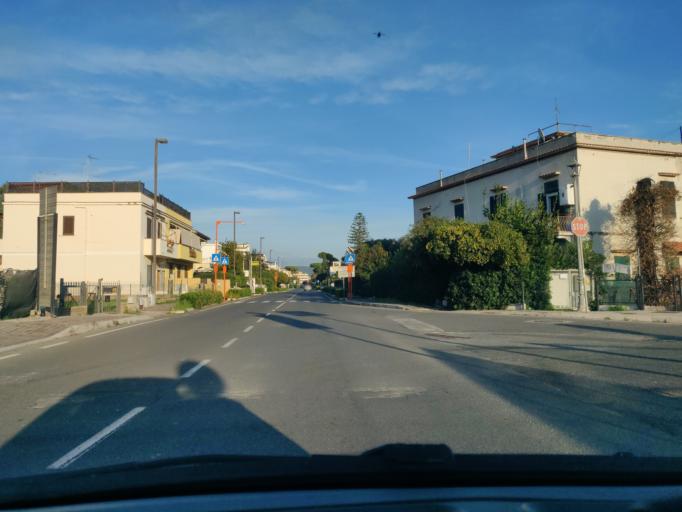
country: IT
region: Latium
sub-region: Citta metropolitana di Roma Capitale
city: Santa Marinella
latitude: 42.0373
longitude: 11.8719
